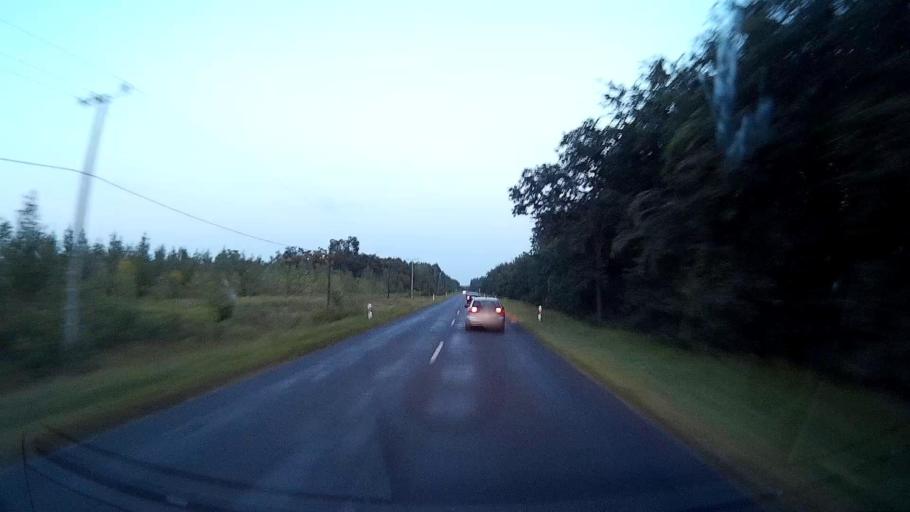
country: HU
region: Pest
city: Cegledbercel
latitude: 47.2040
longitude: 19.6955
